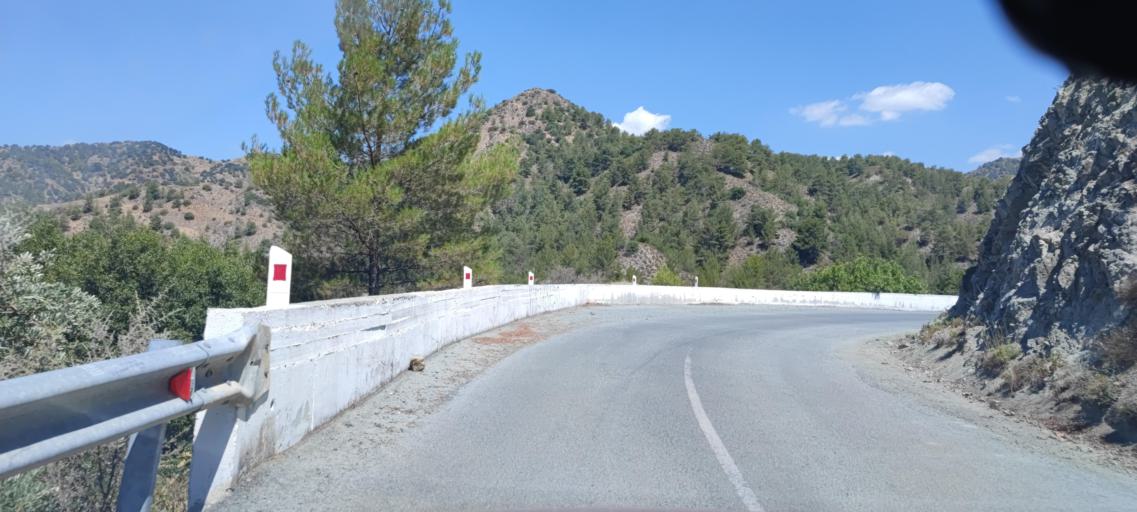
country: CY
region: Lefkosia
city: Kakopetria
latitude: 34.9240
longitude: 32.7940
